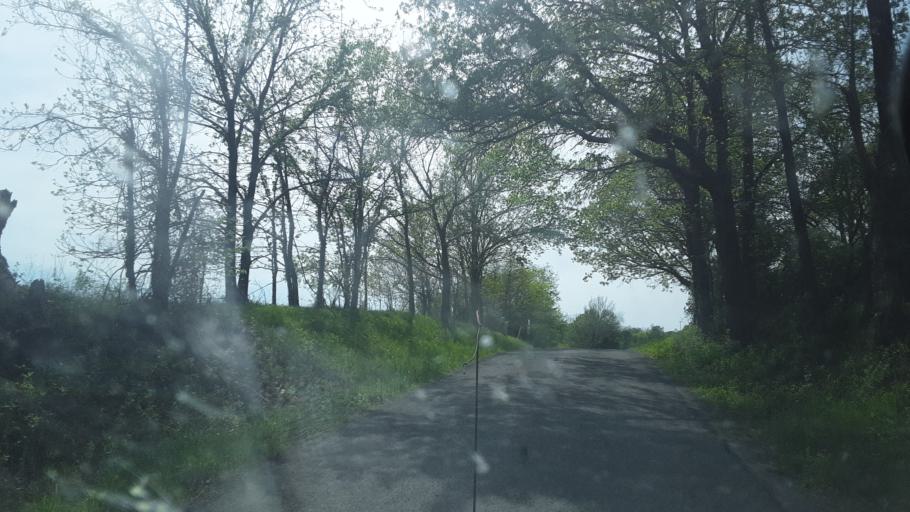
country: US
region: Illinois
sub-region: Jackson County
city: Carbondale
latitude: 37.6809
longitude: -89.2923
